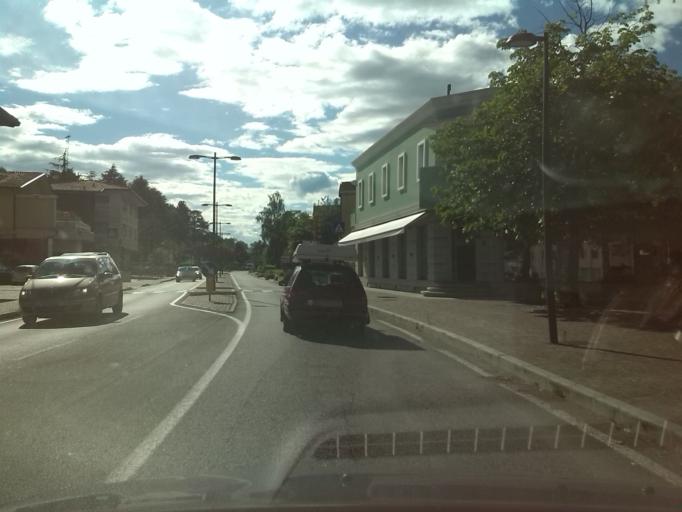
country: IT
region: Friuli Venezia Giulia
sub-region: Provincia di Udine
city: Tricesimo
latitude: 46.1591
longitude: 13.2147
